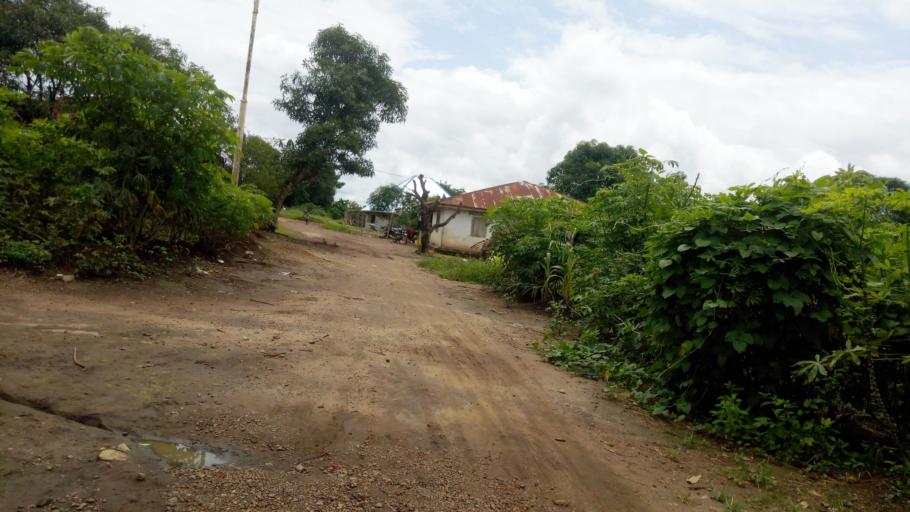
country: SL
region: Northern Province
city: Magburaka
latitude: 8.7172
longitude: -11.9615
